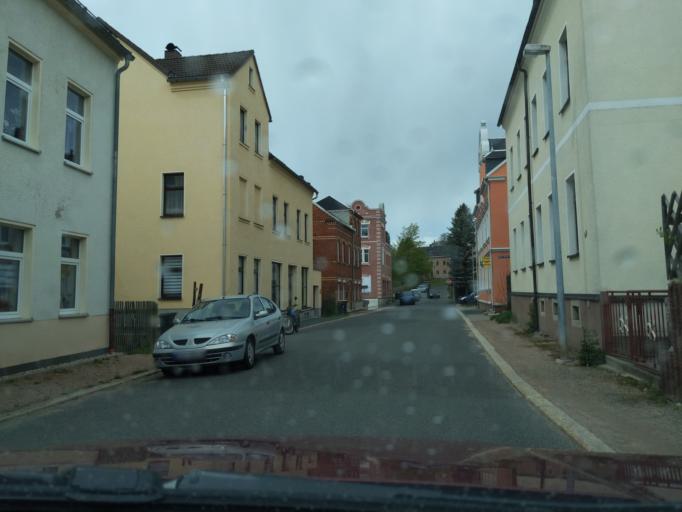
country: DE
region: Saxony
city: Schoenheide
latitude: 50.5038
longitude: 12.5285
